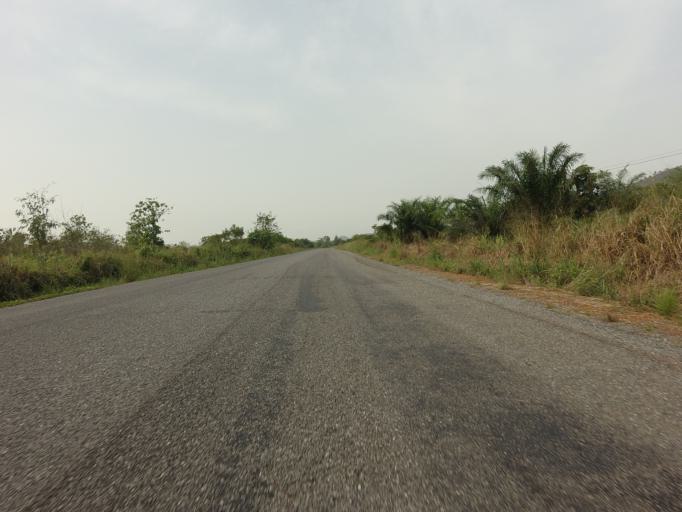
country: GH
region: Volta
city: Ho
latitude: 6.4225
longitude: 0.1882
